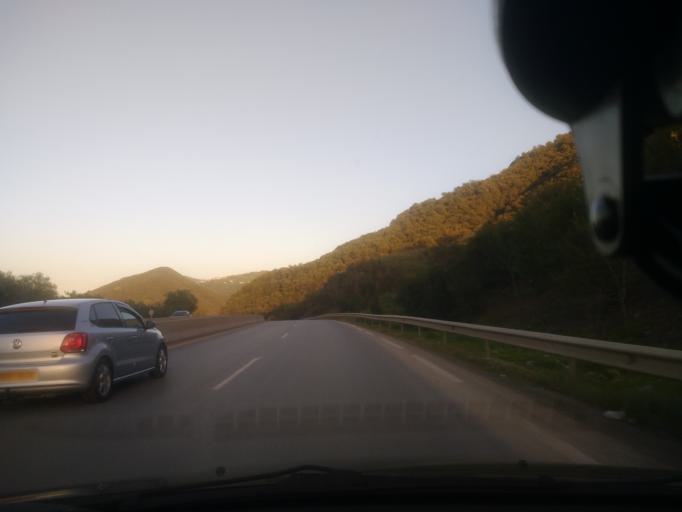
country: DZ
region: Tizi Ouzou
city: Tizi Ouzou
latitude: 36.7486
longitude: 4.0236
